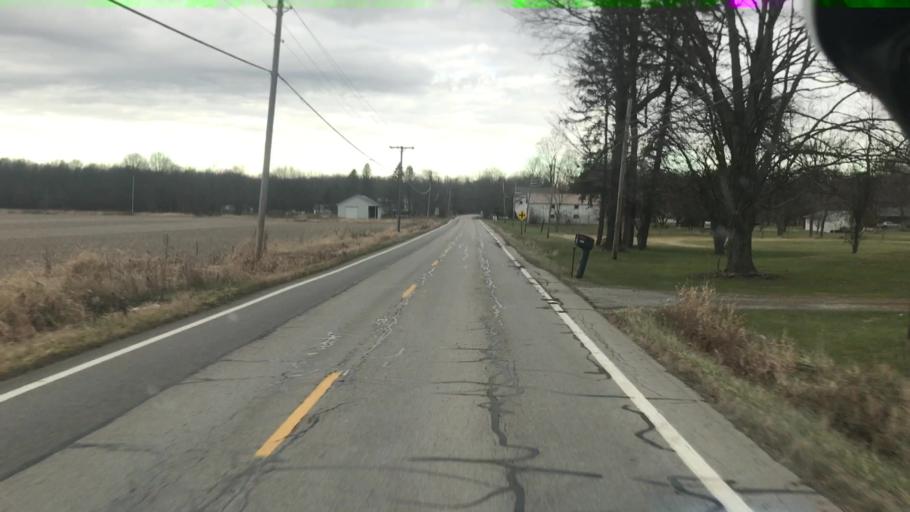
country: US
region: Ohio
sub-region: Trumbull County
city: Newton Falls
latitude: 41.2589
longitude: -80.9783
